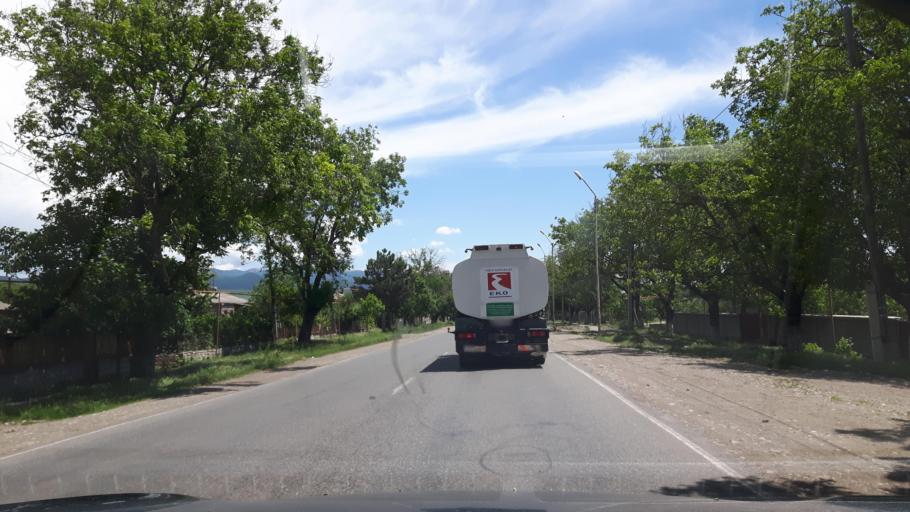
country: GE
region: Kakheti
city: Sagarejo
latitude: 41.7139
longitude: 45.1621
